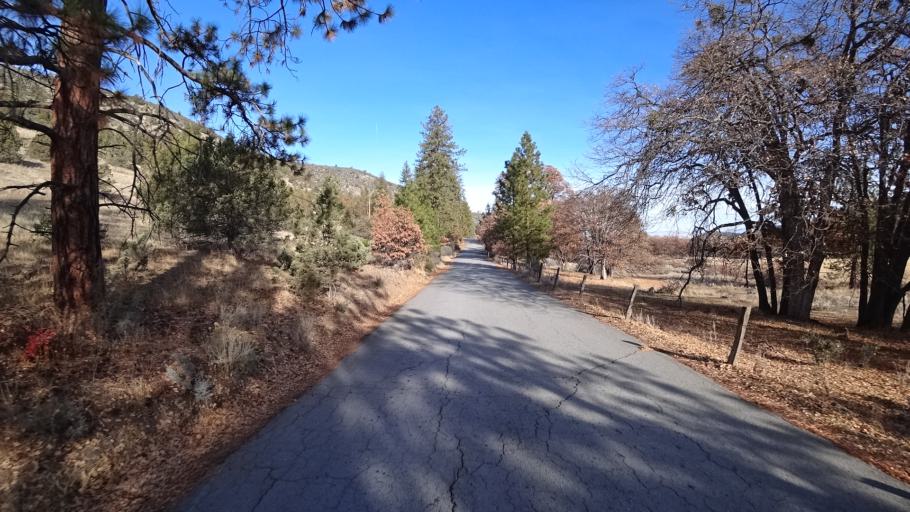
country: US
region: California
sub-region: Siskiyou County
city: Montague
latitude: 41.6150
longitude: -122.5779
